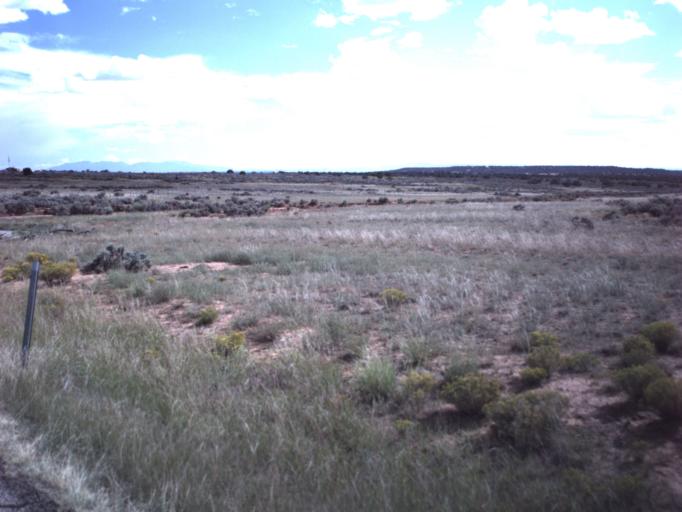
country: US
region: Utah
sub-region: Grand County
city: Moab
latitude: 38.5211
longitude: -109.7324
